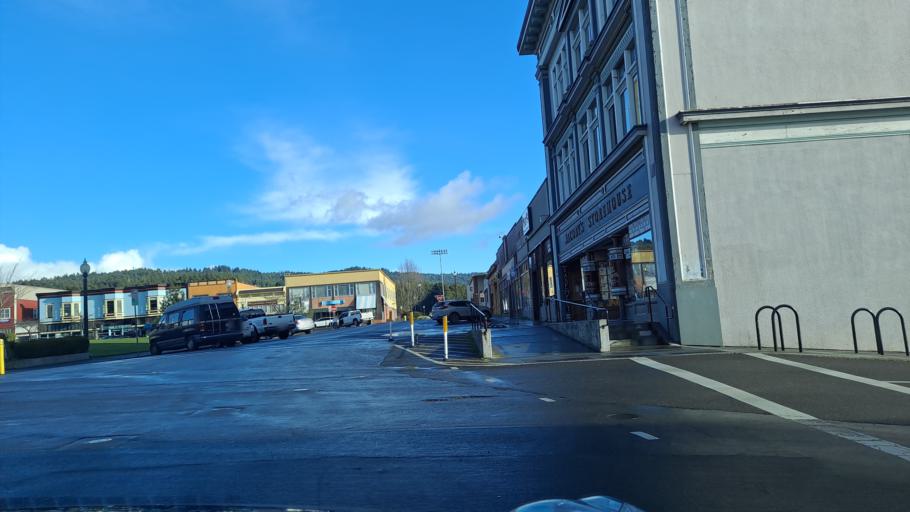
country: US
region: California
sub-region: Humboldt County
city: Arcata
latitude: 40.8683
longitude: -124.0872
